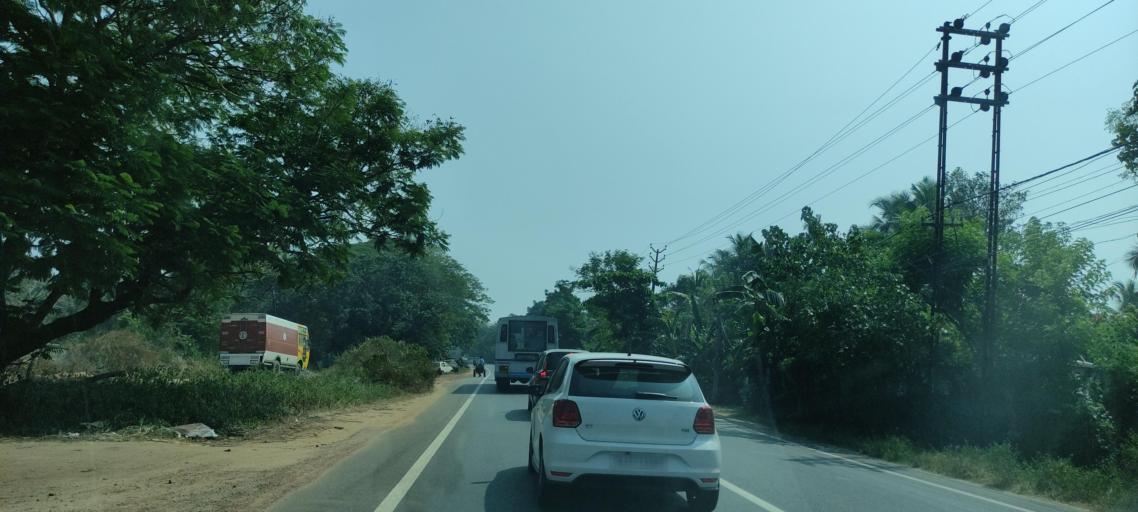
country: IN
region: Kerala
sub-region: Alappuzha
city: Alleppey
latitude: 9.3267
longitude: 76.3767
